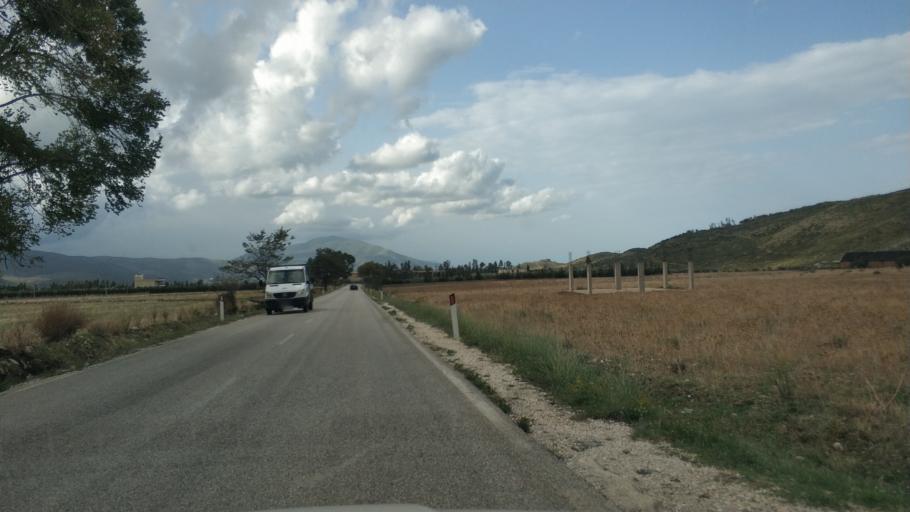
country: AL
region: Vlore
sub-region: Rrethi i Vlores
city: Orikum
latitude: 40.2761
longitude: 19.5071
